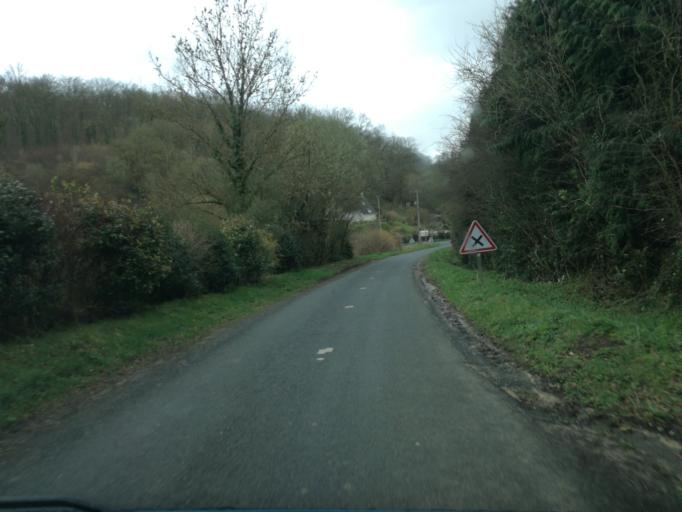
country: FR
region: Haute-Normandie
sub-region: Departement de la Seine-Maritime
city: Saint-Wandrille-Rancon
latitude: 49.5568
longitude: 0.7526
